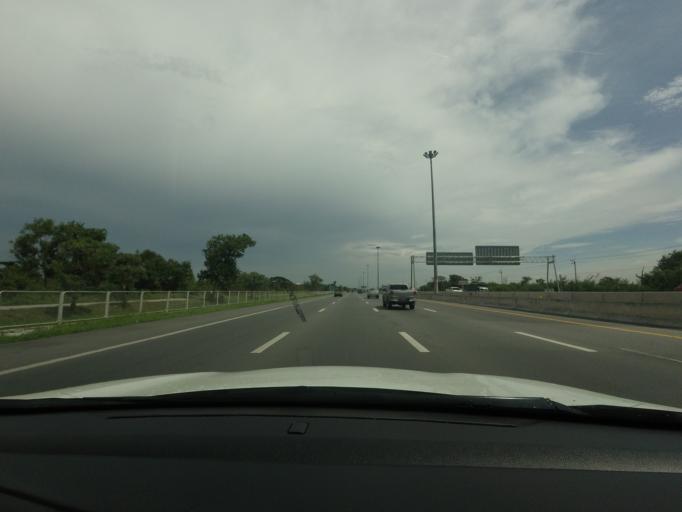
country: TH
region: Pathum Thani
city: Thanyaburi
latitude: 14.0572
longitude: 100.6977
